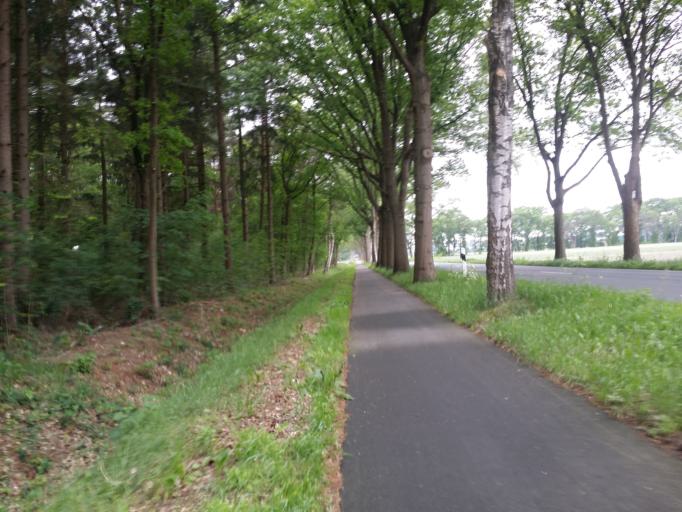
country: DE
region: Lower Saxony
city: Hatten
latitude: 53.0766
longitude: 8.4093
